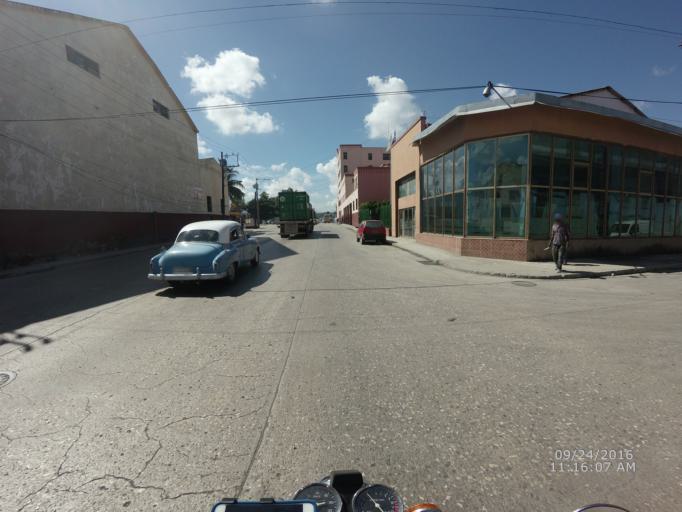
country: CU
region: La Habana
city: La Habana Vieja
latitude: 23.1155
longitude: -82.3592
